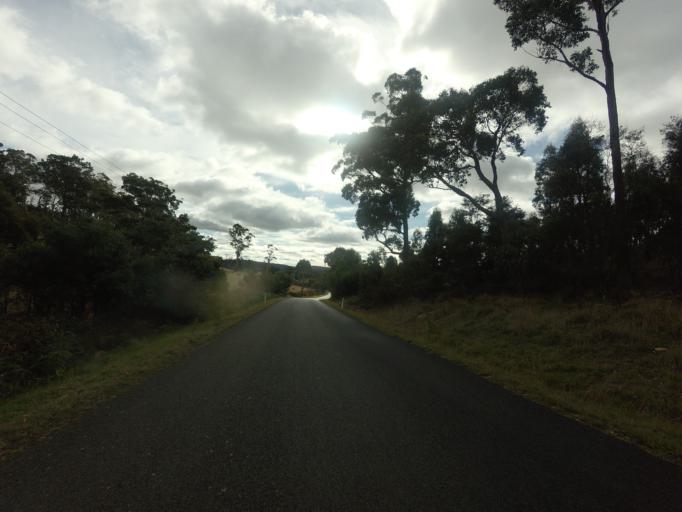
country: AU
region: Tasmania
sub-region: Brighton
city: Bridgewater
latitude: -42.4143
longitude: 147.4086
